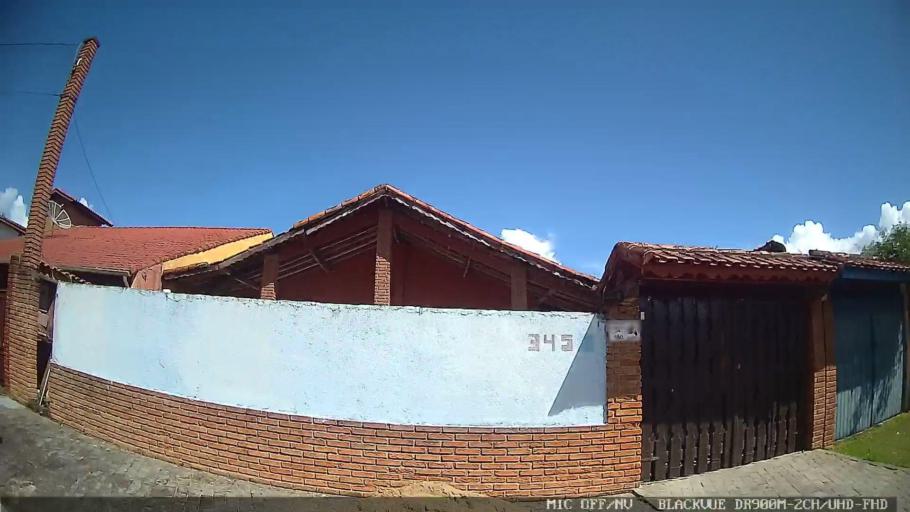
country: BR
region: Sao Paulo
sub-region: Itanhaem
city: Itanhaem
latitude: -24.2320
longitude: -46.8747
